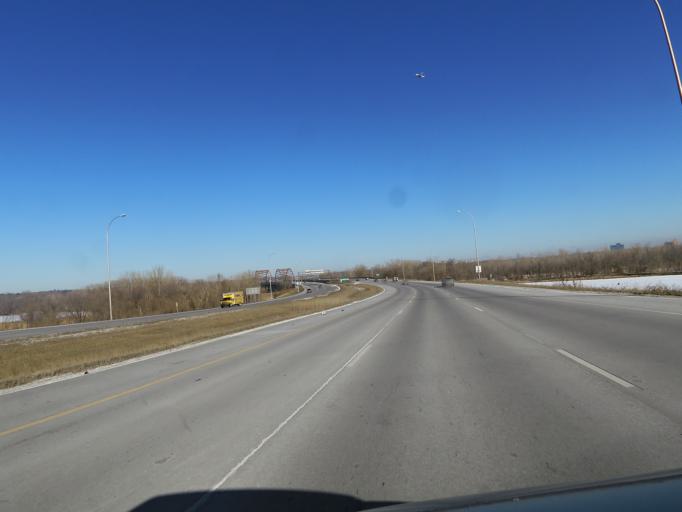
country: US
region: Minnesota
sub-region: Dakota County
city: Eagan
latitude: 44.8216
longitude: -93.2249
